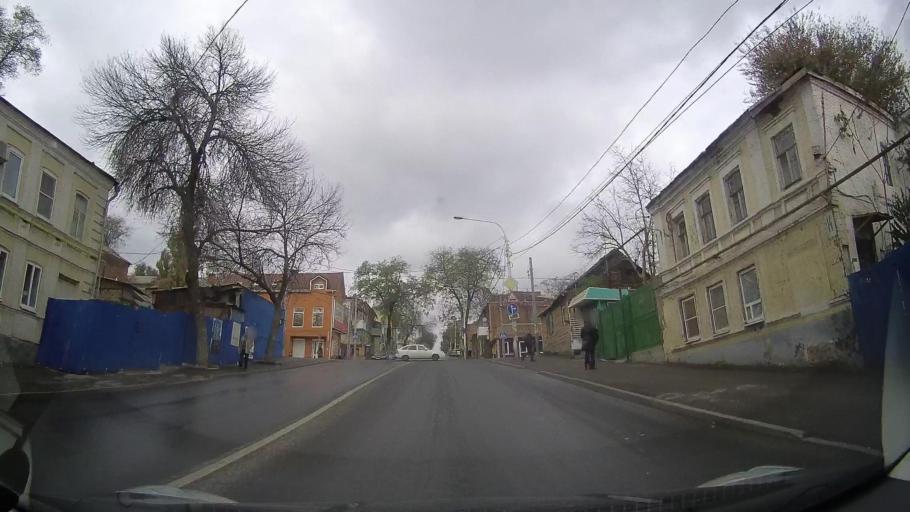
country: RU
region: Rostov
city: Rostov-na-Donu
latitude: 47.2212
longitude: 39.7323
